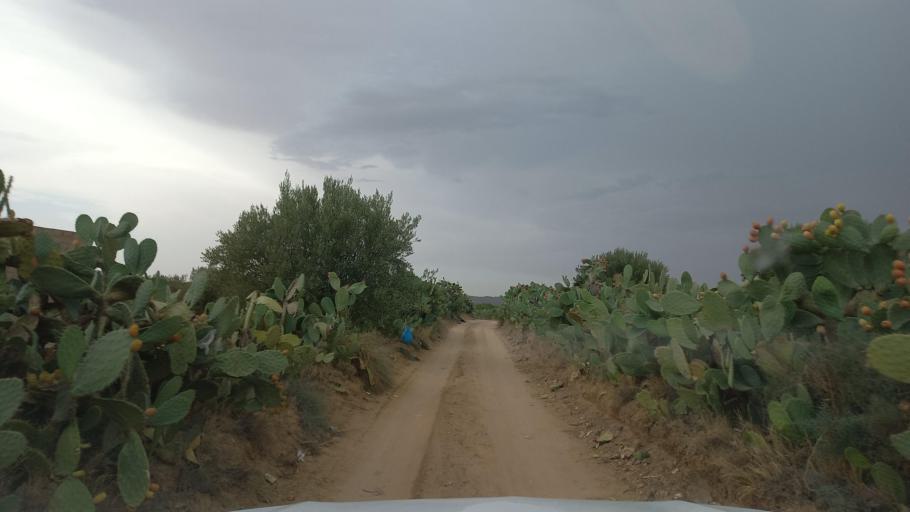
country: TN
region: Al Qasrayn
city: Kasserine
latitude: 35.2400
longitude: 9.0249
